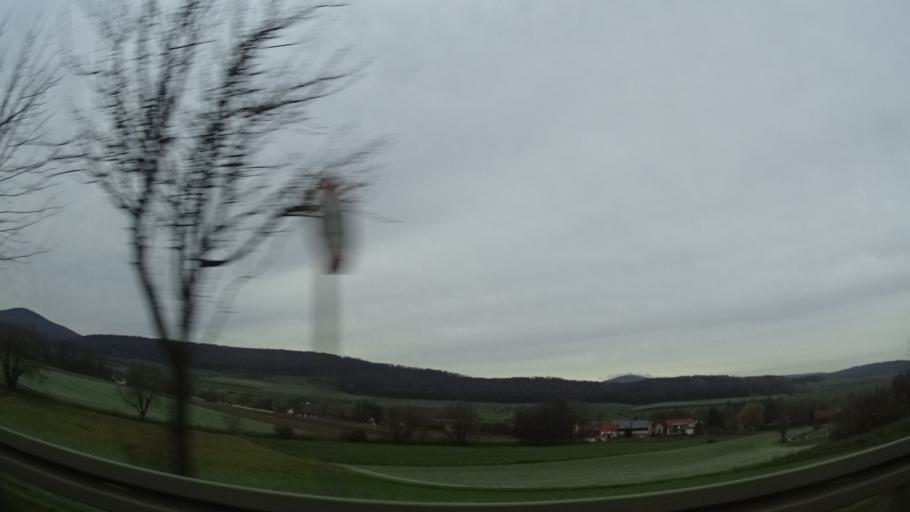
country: DE
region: Thuringia
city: Buttlar
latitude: 50.7372
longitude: 9.9241
